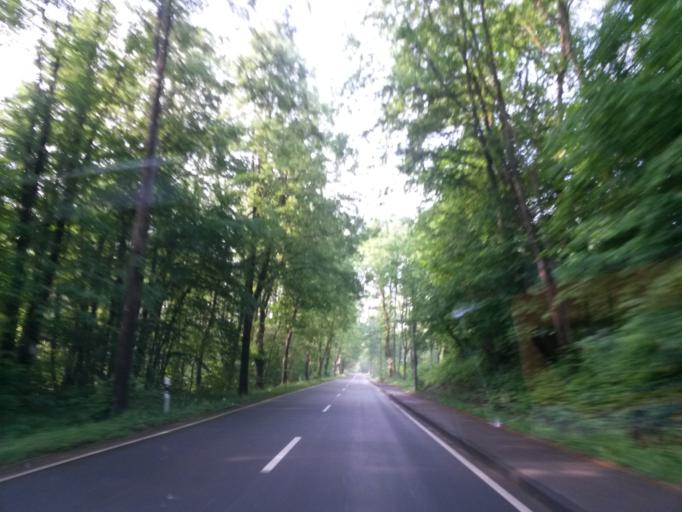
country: DE
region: North Rhine-Westphalia
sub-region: Regierungsbezirk Koln
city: Much
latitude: 50.9011
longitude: 7.4078
